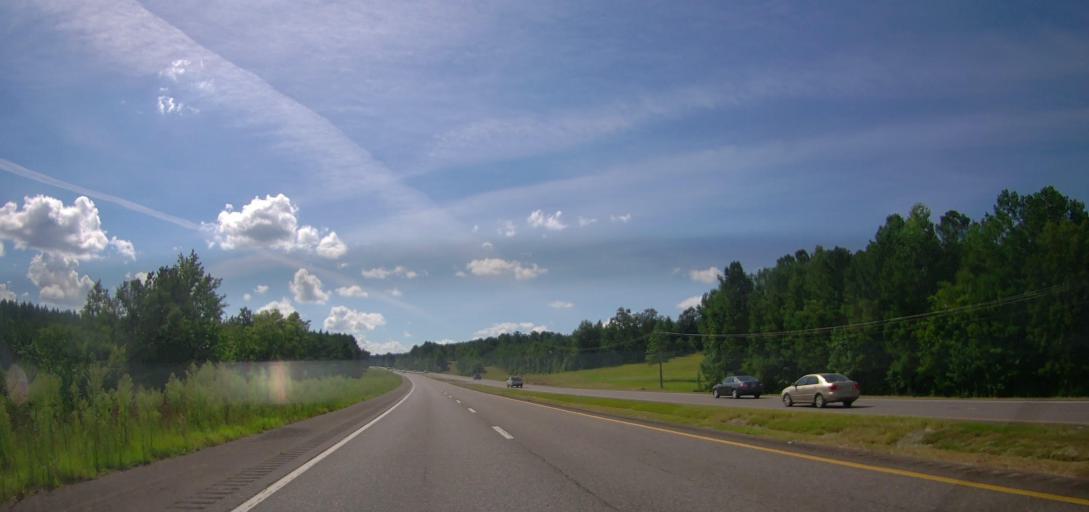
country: US
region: Alabama
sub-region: Tuscaloosa County
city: Northport
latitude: 33.2657
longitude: -87.7145
